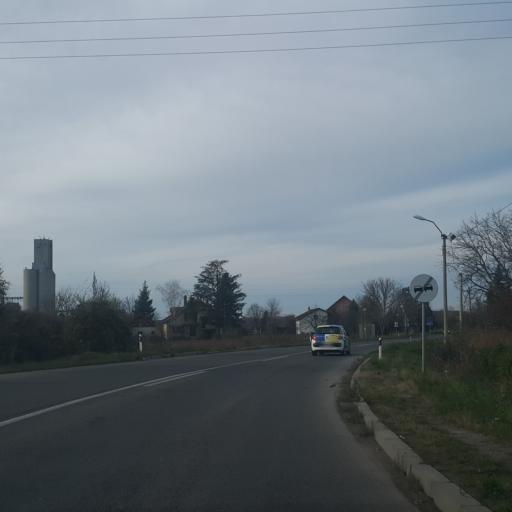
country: RS
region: Central Serbia
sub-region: Kolubarski Okrug
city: Lajkovac
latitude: 44.3679
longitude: 20.1923
